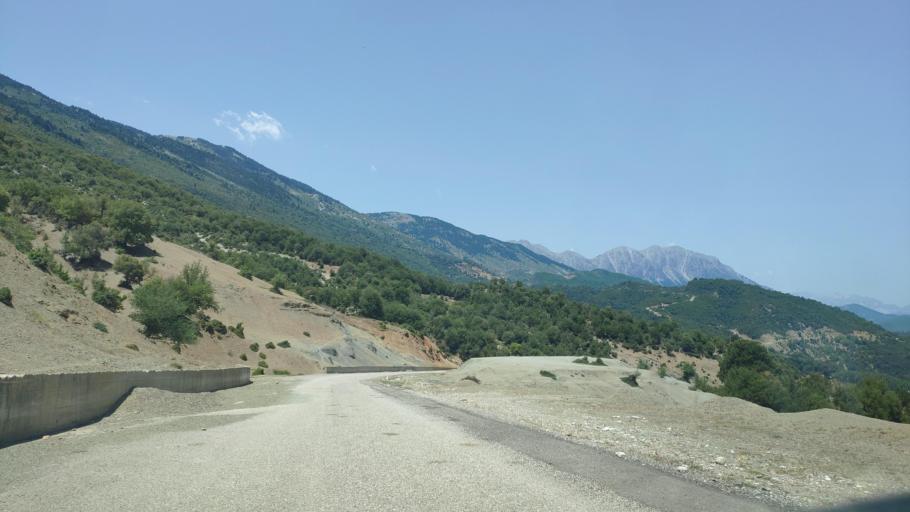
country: GR
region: Thessaly
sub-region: Nomos Kardhitsas
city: Anthiro
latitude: 39.1586
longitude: 21.3833
